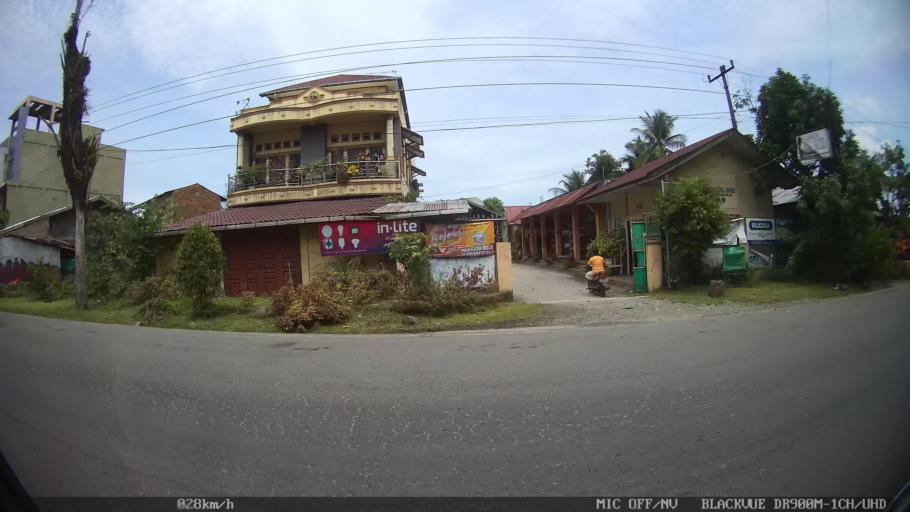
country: ID
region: North Sumatra
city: Sunggal
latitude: 3.5246
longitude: 98.6198
